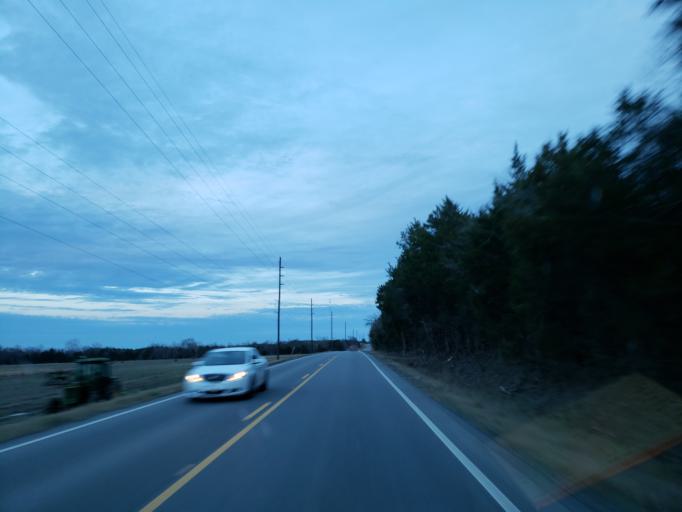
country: US
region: Alabama
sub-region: Sumter County
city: Livingston
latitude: 32.8047
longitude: -88.3074
